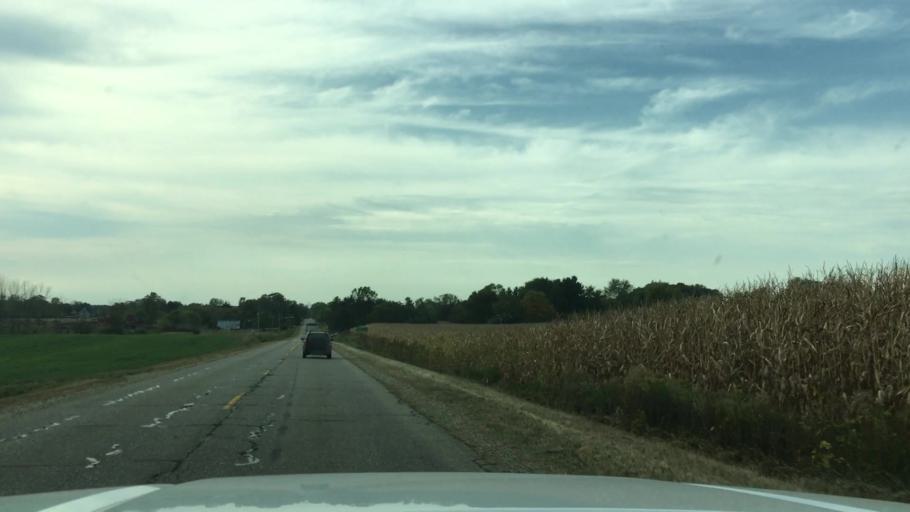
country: US
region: Michigan
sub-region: Ottawa County
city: Hudsonville
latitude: 42.7821
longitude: -85.8579
